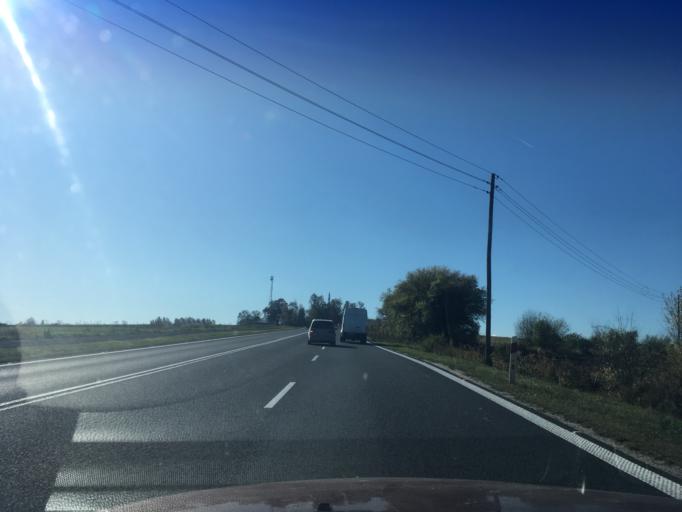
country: DE
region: Saxony
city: Ostritz
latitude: 50.9770
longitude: 14.9440
